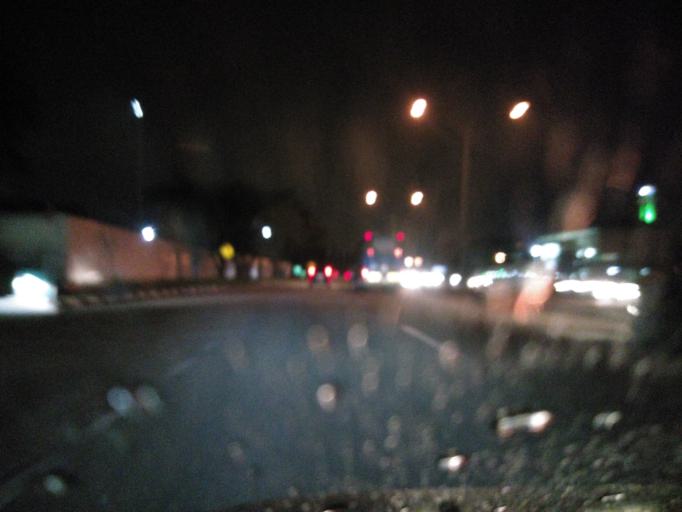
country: MY
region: Penang
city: Perai
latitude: 5.4006
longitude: 100.3993
